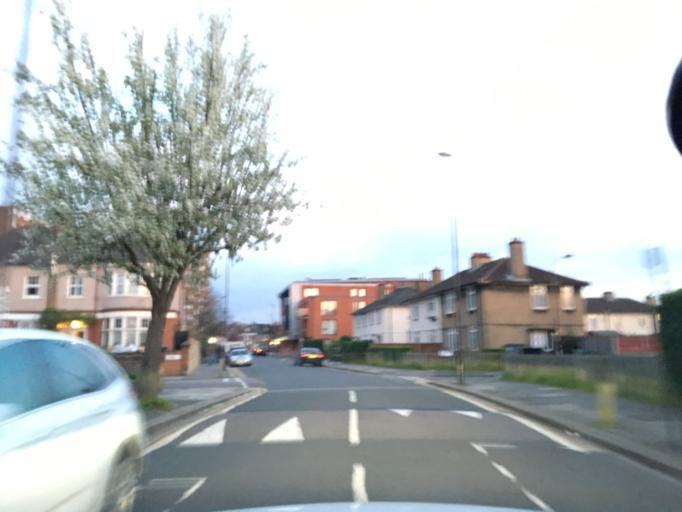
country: GB
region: England
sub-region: Greater London
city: Chislehurst
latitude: 51.4531
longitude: 0.0482
